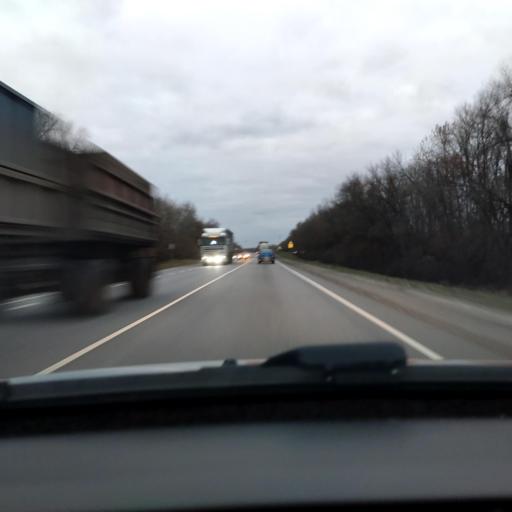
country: RU
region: Lipetsk
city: Borinskoye
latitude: 52.4160
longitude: 39.2511
